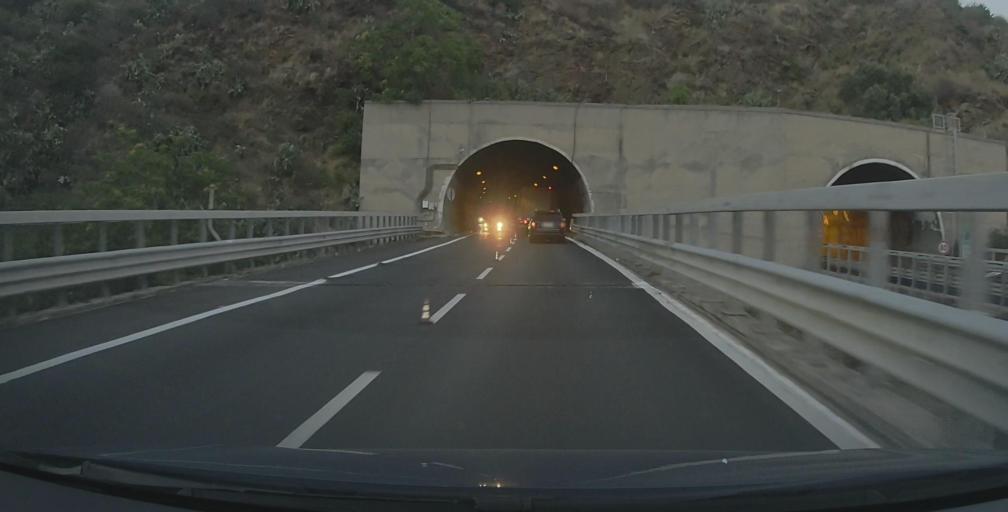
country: IT
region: Sicily
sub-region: Messina
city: Scaletta Zanclea
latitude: 38.0511
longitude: 15.4697
